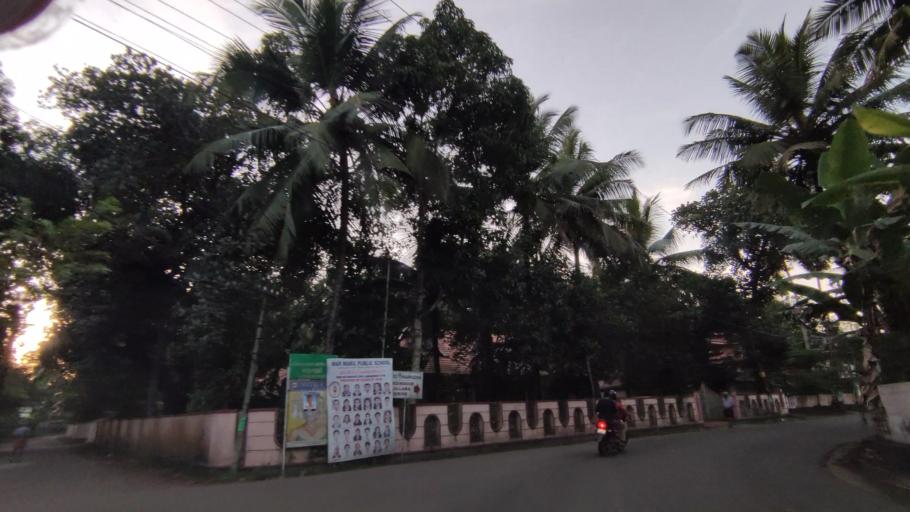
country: IN
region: Kerala
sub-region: Kottayam
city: Kottayam
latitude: 9.6534
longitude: 76.5068
